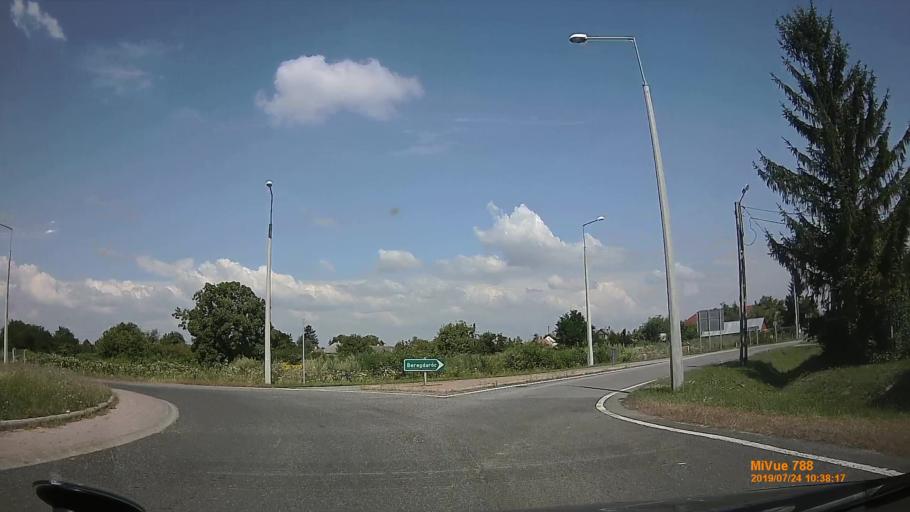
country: HU
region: Szabolcs-Szatmar-Bereg
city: Tarpa
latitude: 48.1593
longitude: 22.5427
